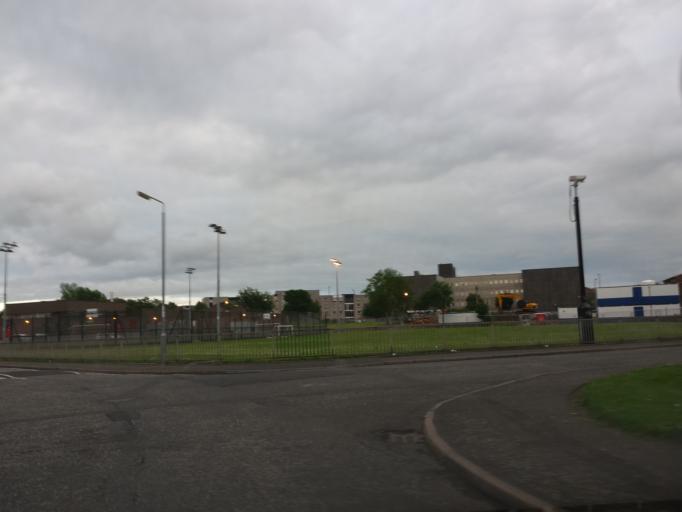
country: GB
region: Scotland
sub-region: South Ayrshire
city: Ayr
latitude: 55.4683
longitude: -4.6254
